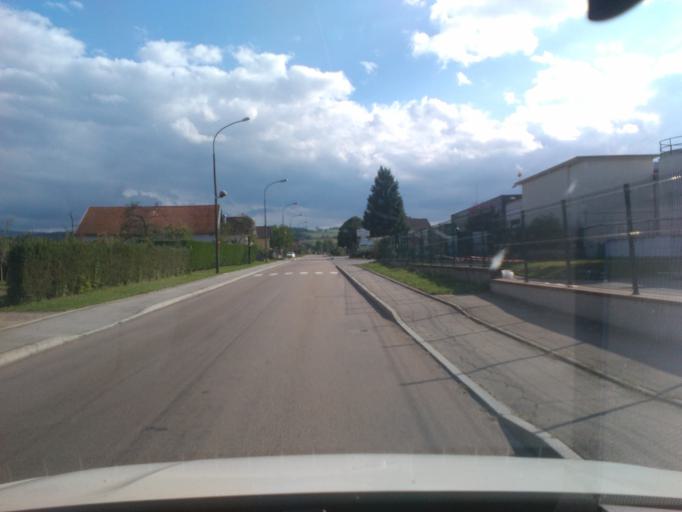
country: FR
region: Lorraine
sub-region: Departement des Vosges
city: Corcieux
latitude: 48.1796
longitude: 6.8841
